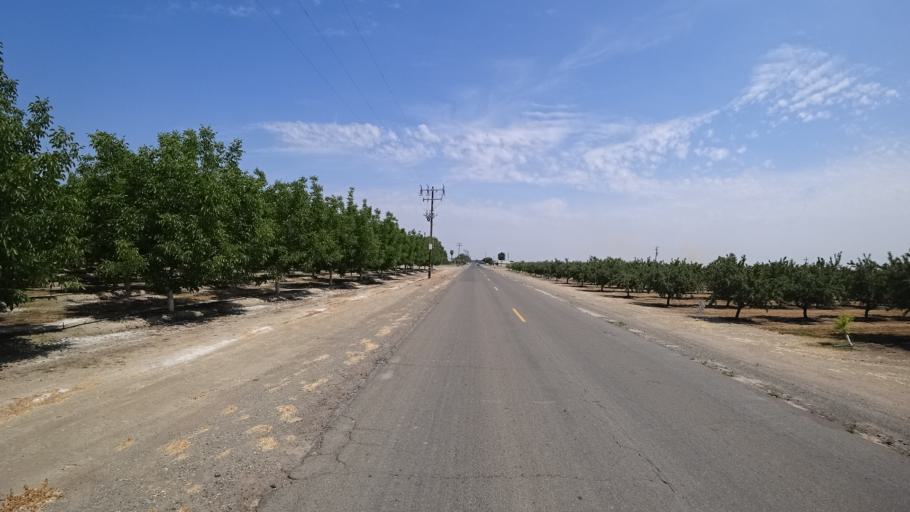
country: US
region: California
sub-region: Fresno County
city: Laton
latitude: 36.3852
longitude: -119.7450
